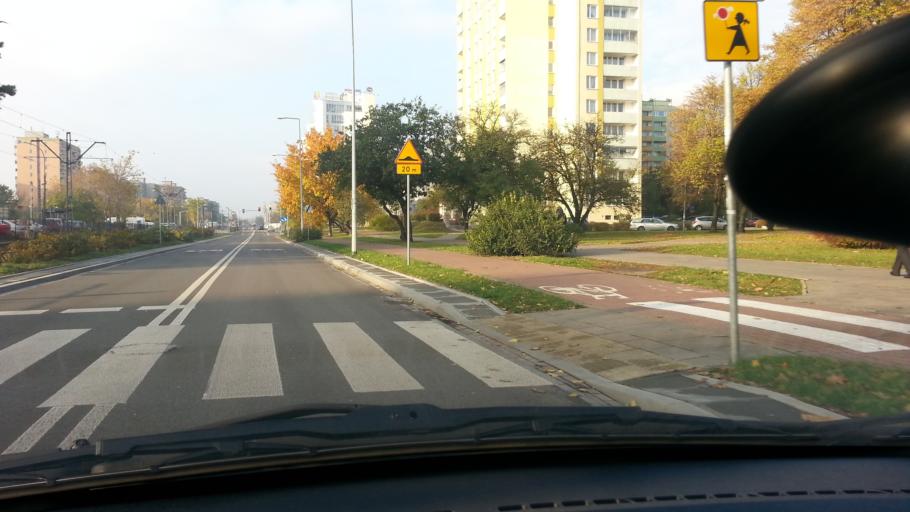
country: PL
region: Masovian Voivodeship
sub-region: Warszawa
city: Targowek
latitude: 52.2863
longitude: 21.0322
